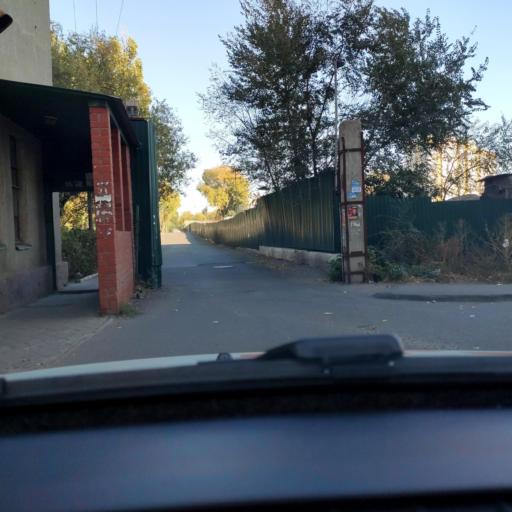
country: RU
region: Voronezj
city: Voronezh
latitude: 51.6443
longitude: 39.1639
